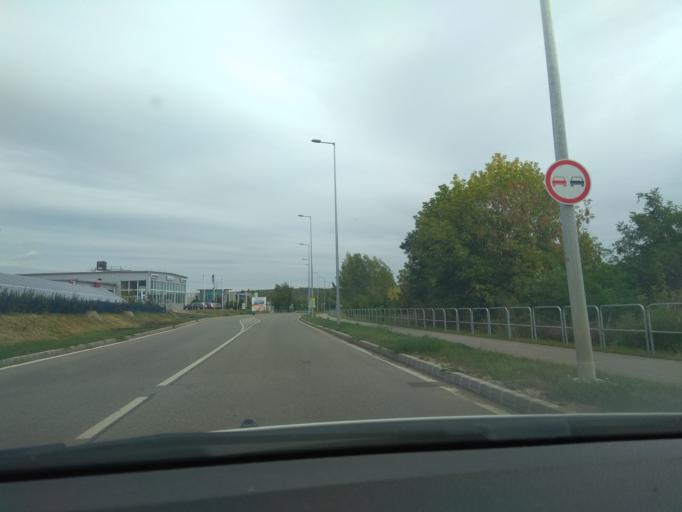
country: HU
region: Heves
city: Eger
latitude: 47.8709
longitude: 20.3862
